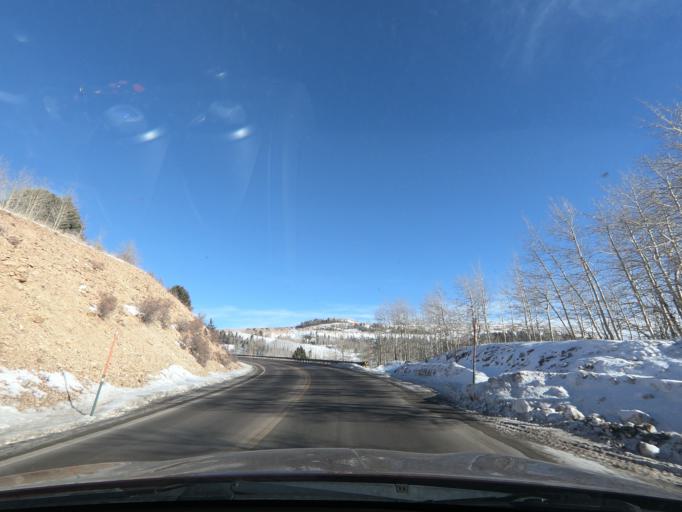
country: US
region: Colorado
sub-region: Teller County
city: Cripple Creek
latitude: 38.7509
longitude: -105.1642
